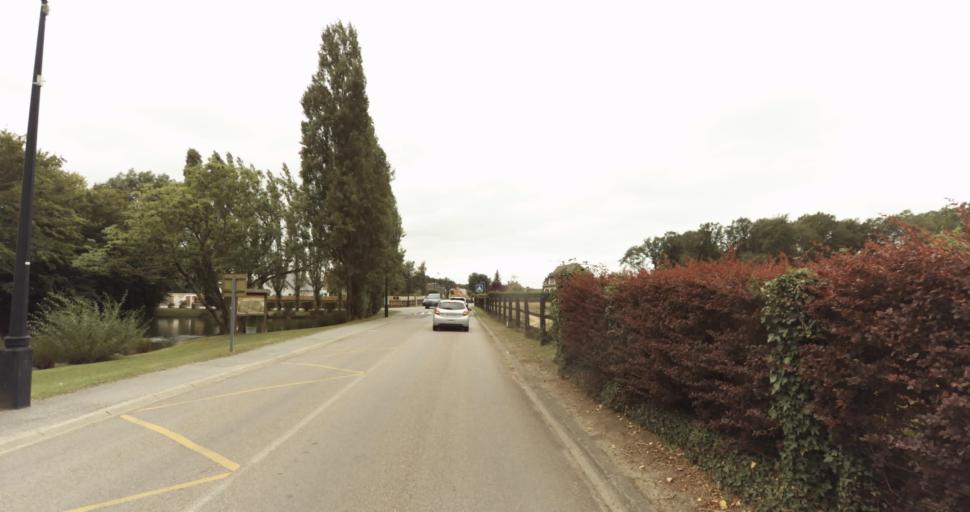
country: FR
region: Haute-Normandie
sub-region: Departement de l'Eure
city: Gravigny
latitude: 49.0374
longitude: 1.2045
